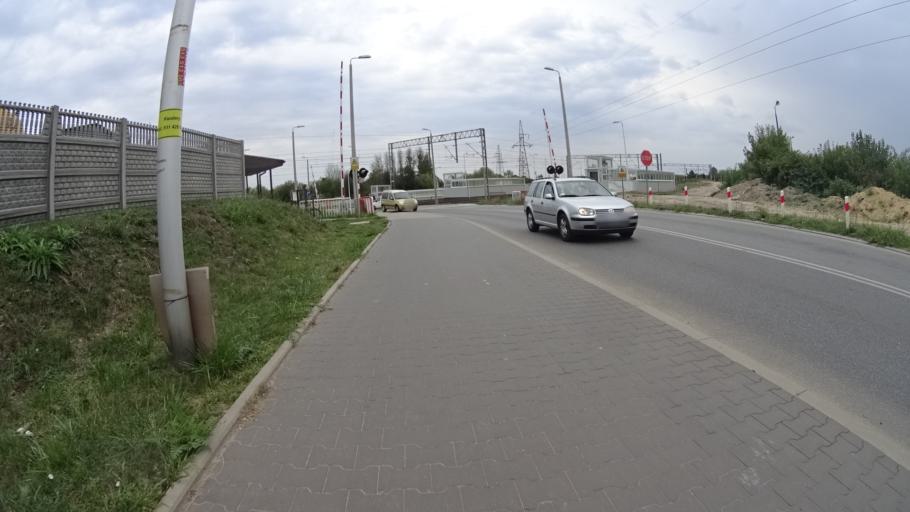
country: PL
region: Masovian Voivodeship
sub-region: Powiat pruszkowski
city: Otrebusy
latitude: 52.1576
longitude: 20.7651
